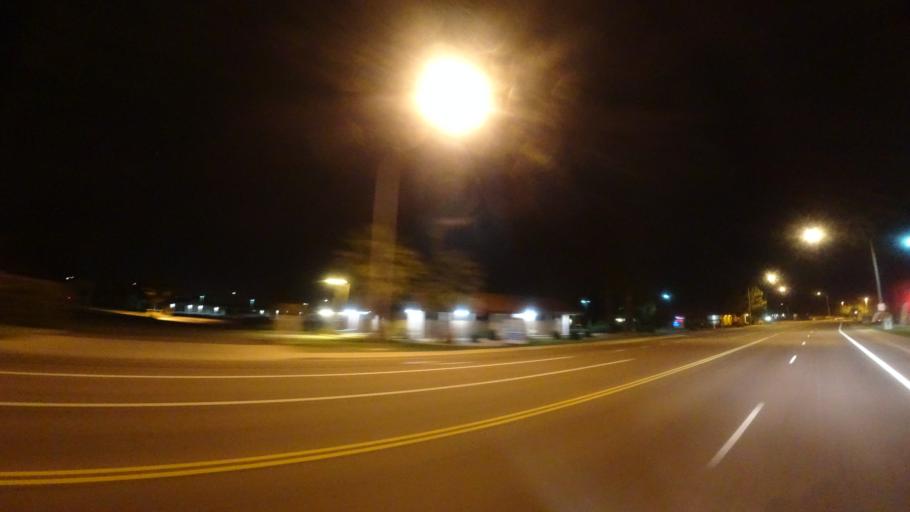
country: US
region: Arizona
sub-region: Maricopa County
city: Gilbert
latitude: 33.4150
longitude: -111.6954
